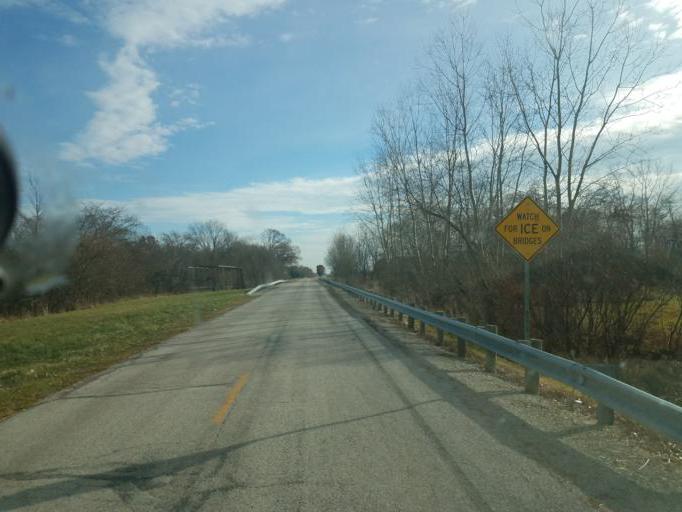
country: US
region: Ohio
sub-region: Crawford County
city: Bucyrus
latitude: 40.6893
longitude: -82.9464
